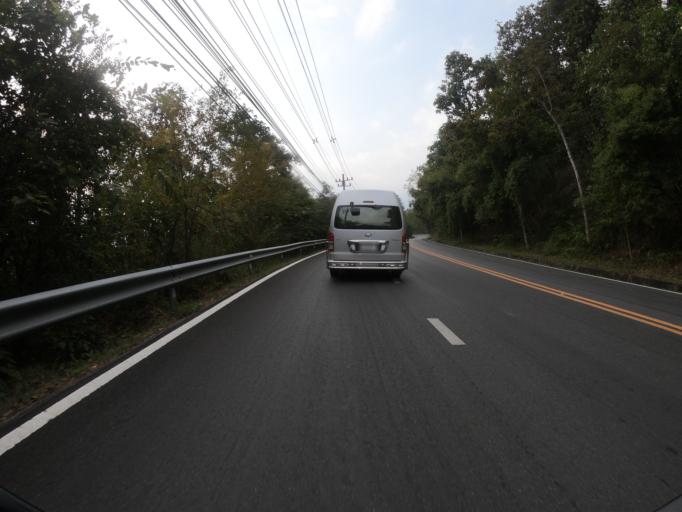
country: TH
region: Chiang Mai
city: Chiang Mai
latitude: 18.8073
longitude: 98.9377
